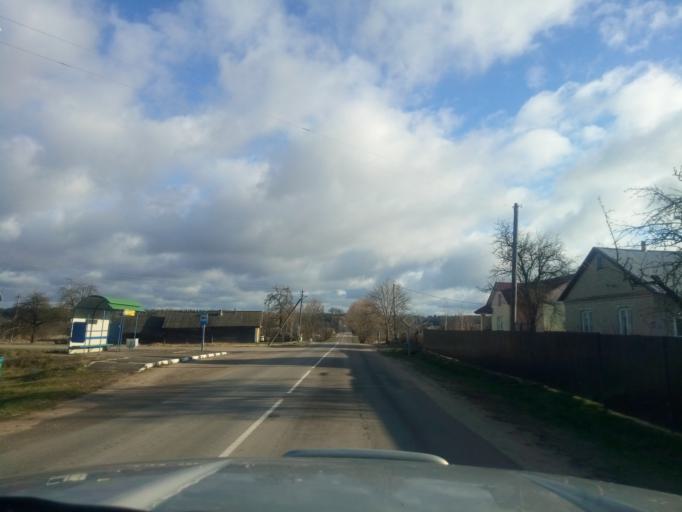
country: BY
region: Minsk
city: Tsimkavichy
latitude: 53.1755
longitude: 26.9600
